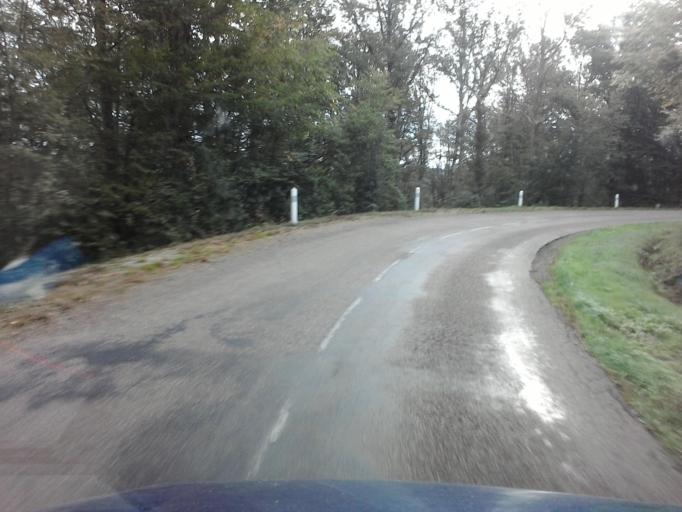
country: FR
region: Bourgogne
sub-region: Departement de la Nievre
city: Lormes
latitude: 47.2060
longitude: 3.8449
